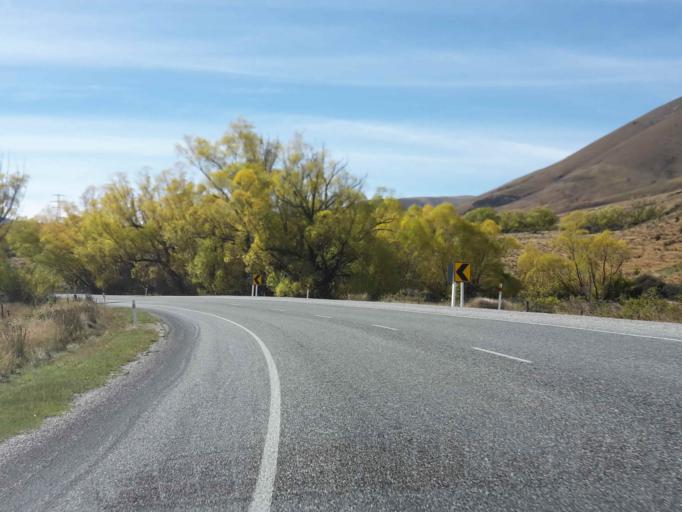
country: NZ
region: Otago
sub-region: Queenstown-Lakes District
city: Wanaka
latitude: -44.5619
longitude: 169.6897
